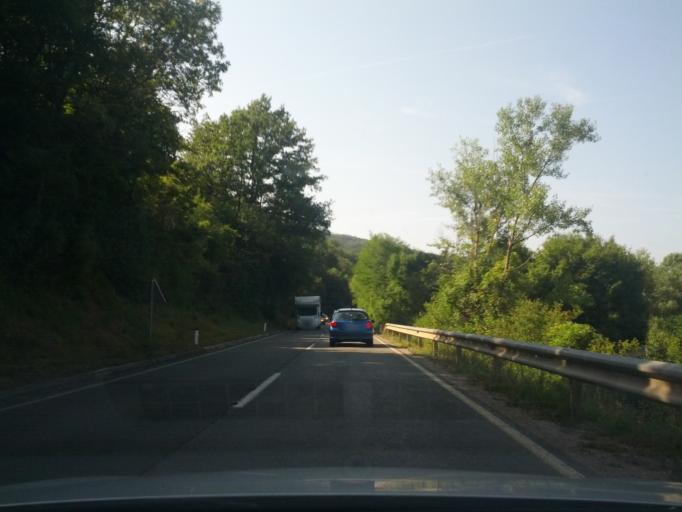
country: SI
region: Izola-Isola
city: Jagodje
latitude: 45.4905
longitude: 13.6767
